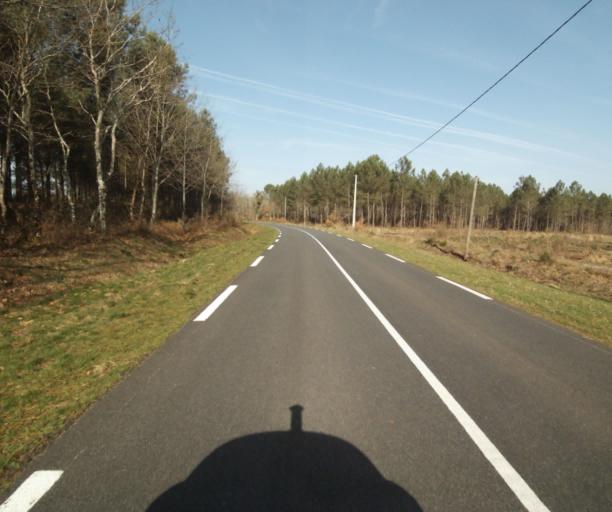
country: FR
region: Aquitaine
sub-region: Departement de la Gironde
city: Grignols
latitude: 44.2076
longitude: -0.1558
